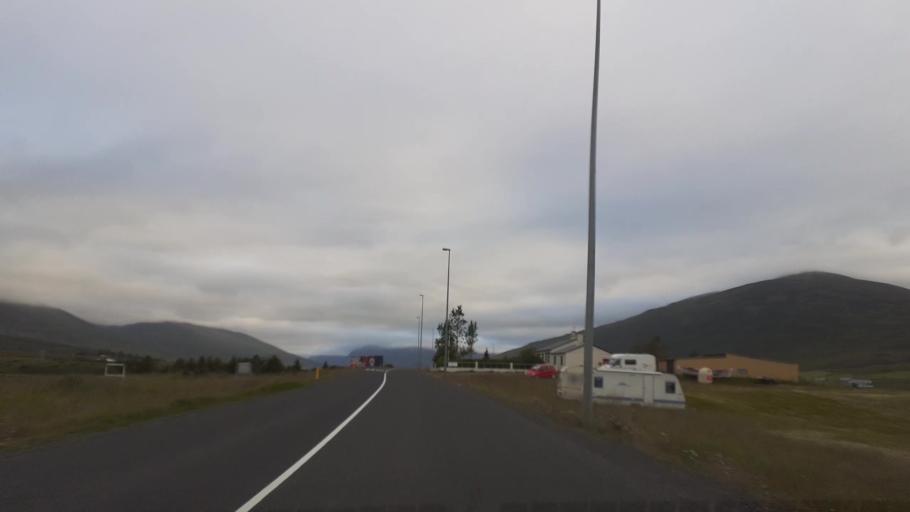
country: IS
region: Northeast
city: Dalvik
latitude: 65.9653
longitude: -18.5329
